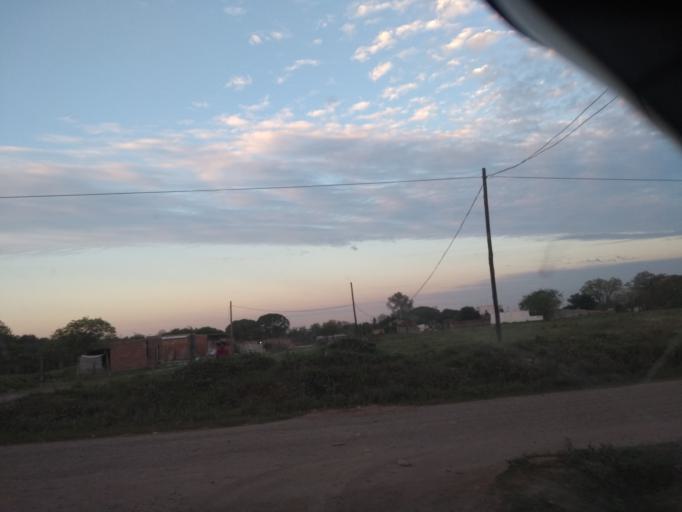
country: AR
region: Chaco
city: Fontana
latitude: -27.4101
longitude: -59.0522
